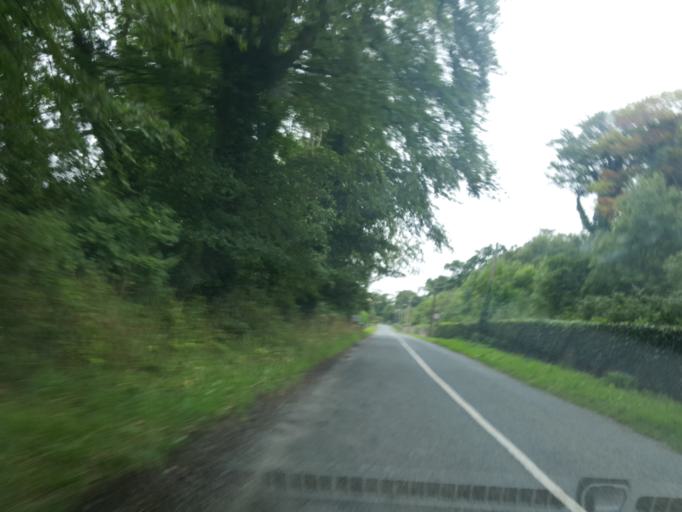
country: IE
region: Leinster
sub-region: Kildare
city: Kilcullen
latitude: 53.1193
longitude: -6.6828
